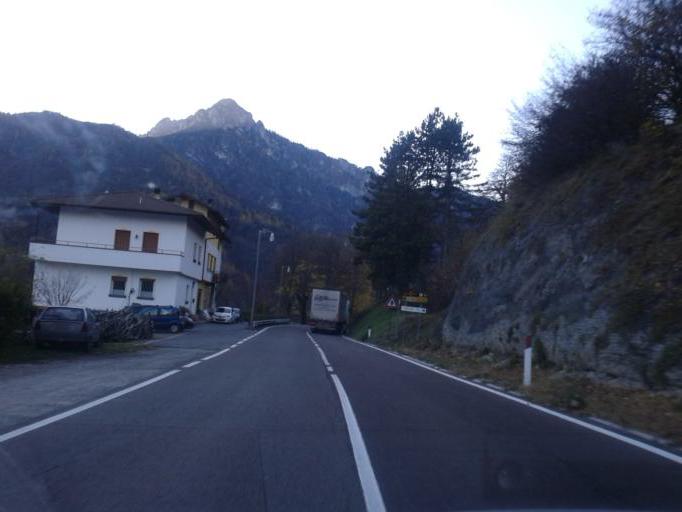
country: IT
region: Trentino-Alto Adige
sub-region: Provincia di Trento
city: Molina di Ledro
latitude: 45.8802
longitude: 10.7530
